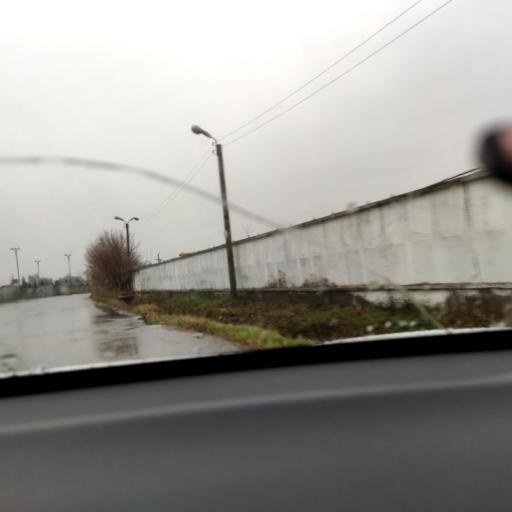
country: RU
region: Tatarstan
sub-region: Gorod Kazan'
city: Kazan
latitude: 55.8658
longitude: 49.1092
